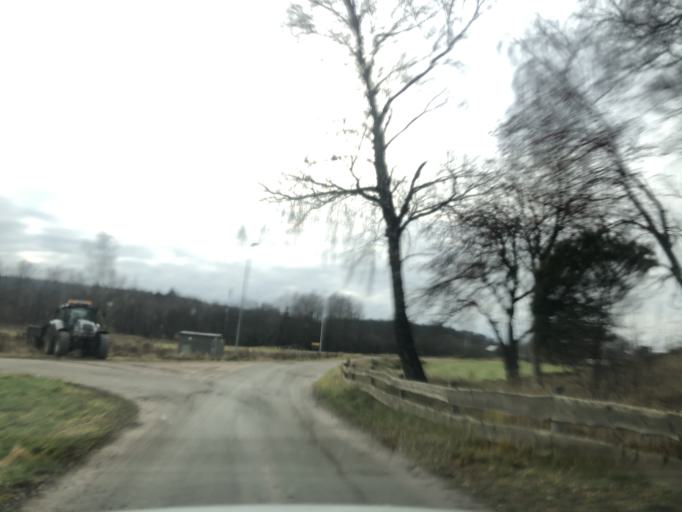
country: SE
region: Vaestra Goetaland
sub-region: Boras Kommun
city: Dalsjofors
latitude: 57.8302
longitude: 13.1723
